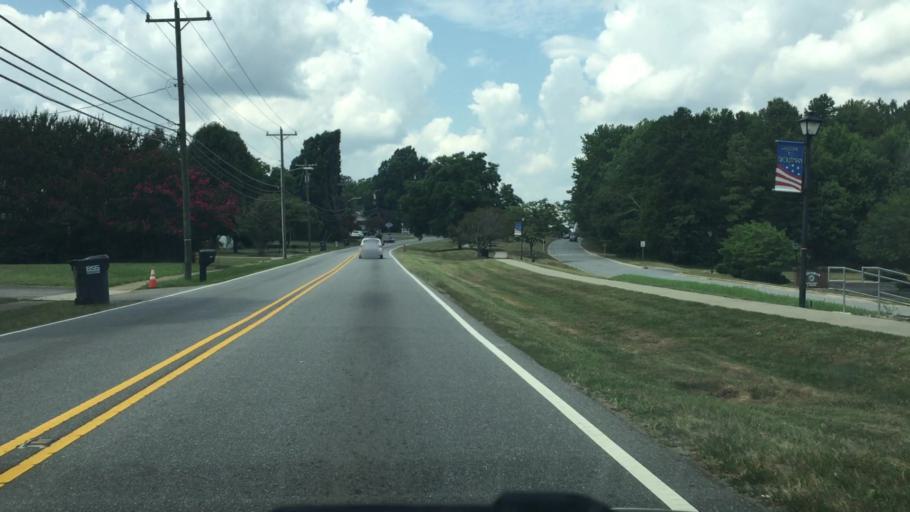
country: US
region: North Carolina
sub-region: Iredell County
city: Troutman
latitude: 35.7065
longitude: -80.8927
